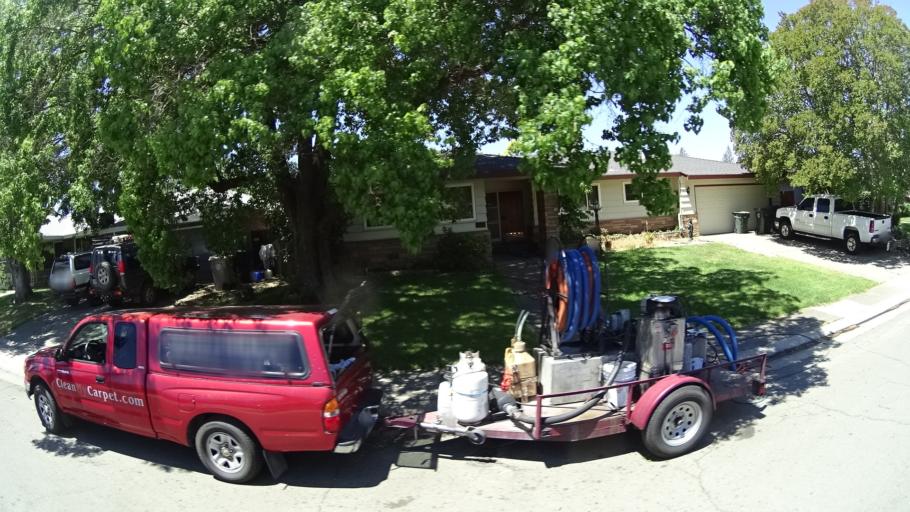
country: US
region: California
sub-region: Sacramento County
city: Parkway
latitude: 38.5112
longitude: -121.5136
